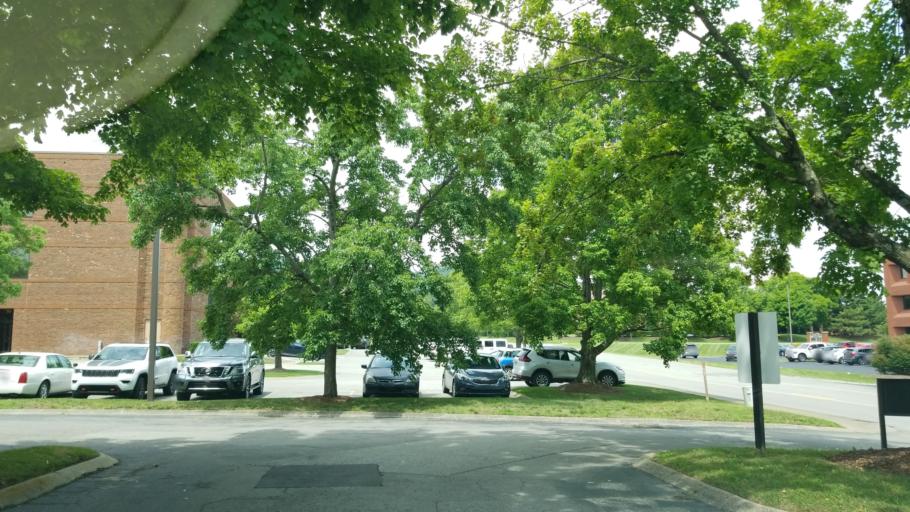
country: US
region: Tennessee
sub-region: Williamson County
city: Brentwood
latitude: 36.0333
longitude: -86.8025
